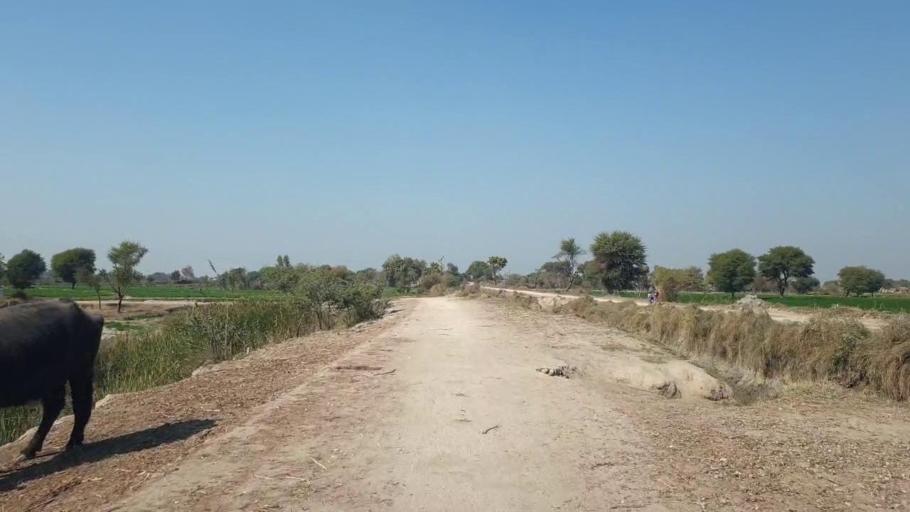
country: PK
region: Sindh
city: Shahdadpur
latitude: 25.9659
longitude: 68.6183
